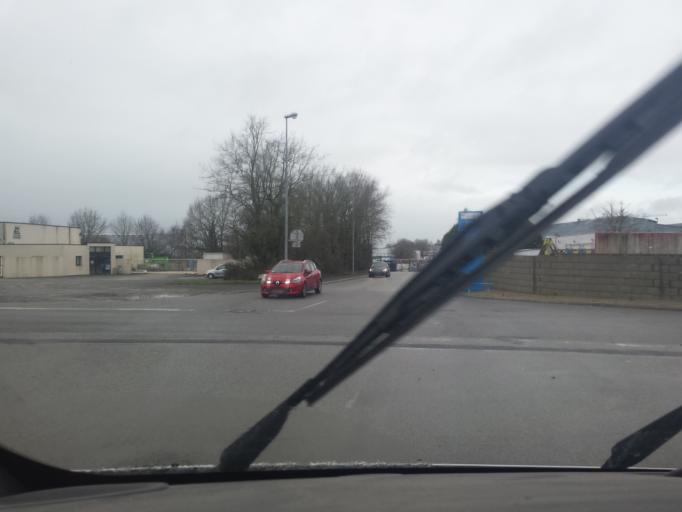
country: FR
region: Pays de la Loire
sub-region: Departement de la Vendee
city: La Roche-sur-Yon
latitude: 46.6397
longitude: -1.4104
